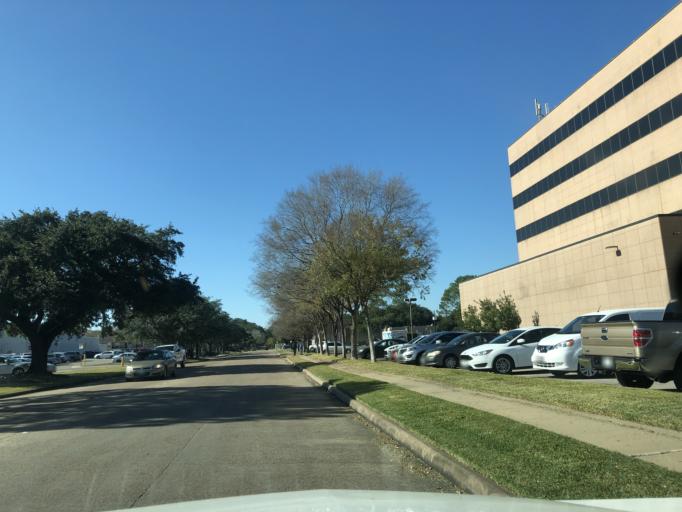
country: US
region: Texas
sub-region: Harris County
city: Bellaire
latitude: 29.6752
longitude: -95.4939
